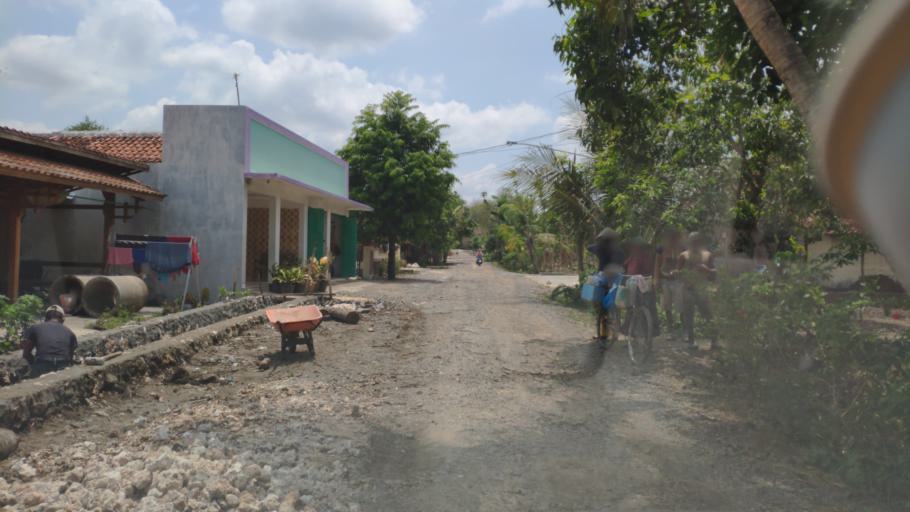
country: ID
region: Central Java
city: Ngablak
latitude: -7.0278
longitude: 111.3883
